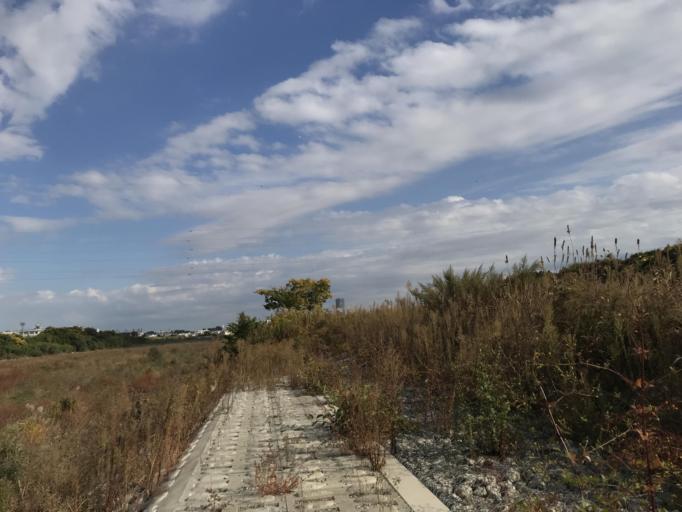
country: JP
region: Tokyo
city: Chofugaoka
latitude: 35.6167
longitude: 139.6015
